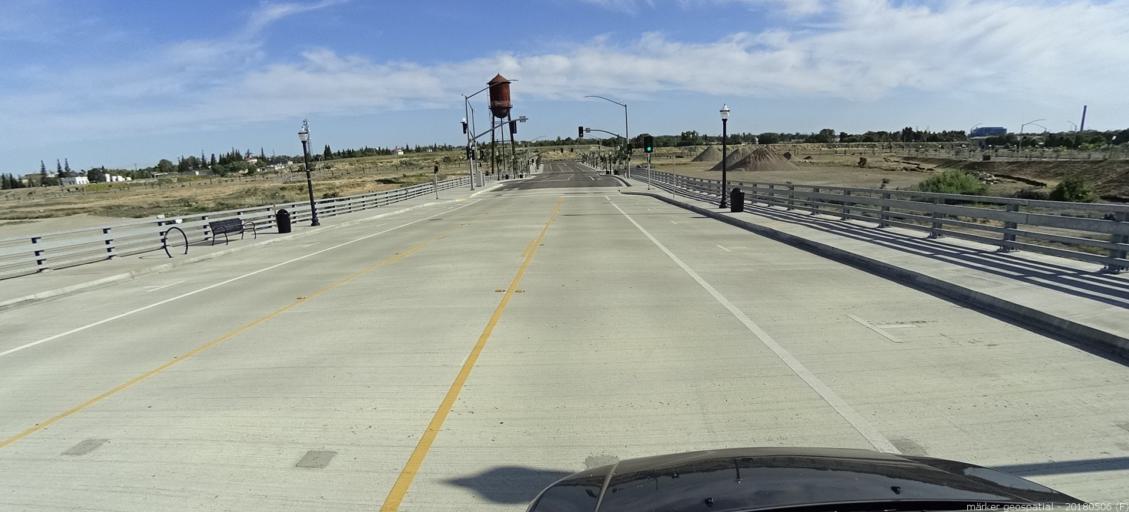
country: US
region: California
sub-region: Sacramento County
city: Sacramento
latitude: 38.5874
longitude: -121.4975
